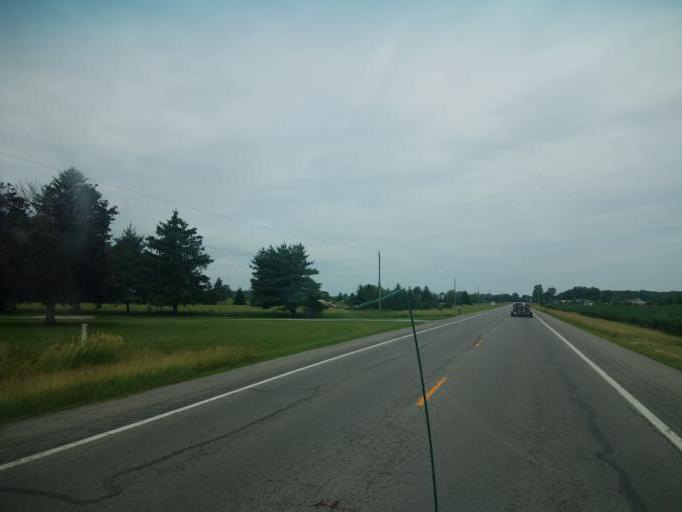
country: US
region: Ohio
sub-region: Hardin County
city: Ada
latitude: 40.7286
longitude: -83.7890
